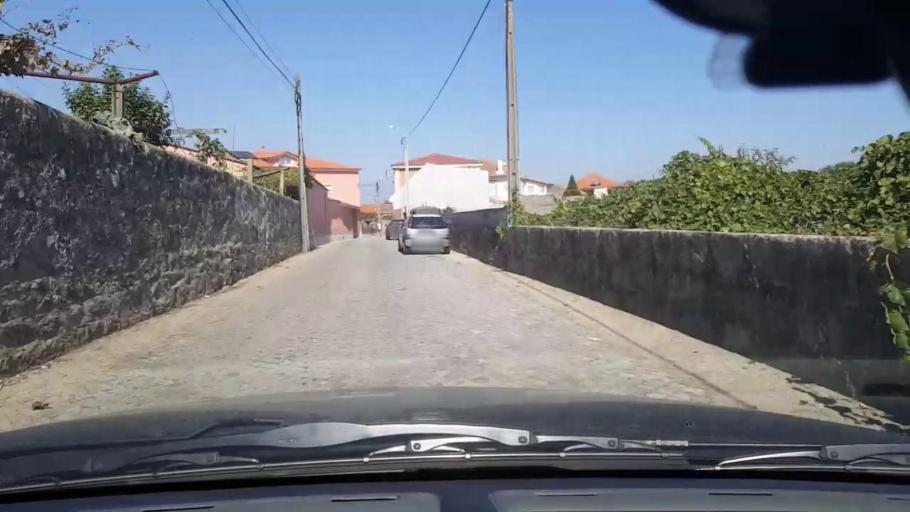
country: PT
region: Porto
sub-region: Matosinhos
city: Lavra
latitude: 41.2655
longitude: -8.6963
